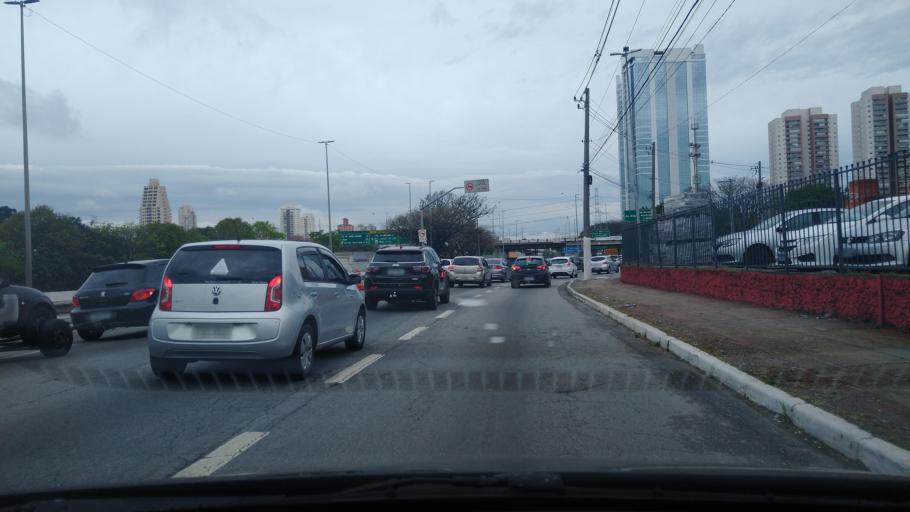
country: SA
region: Ar Riyad
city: Ad Dilam
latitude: 23.5158
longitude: 46.6690
